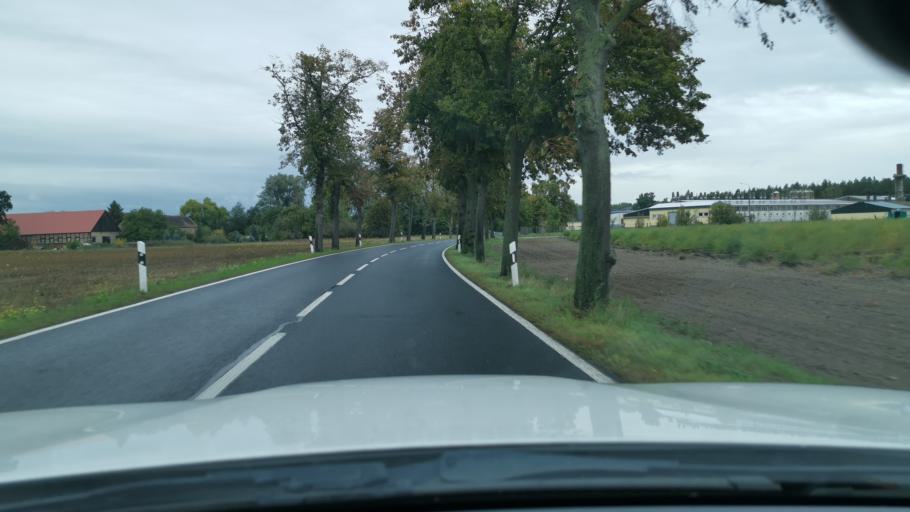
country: DE
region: Brandenburg
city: Beelitz
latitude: 52.1362
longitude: 12.9929
